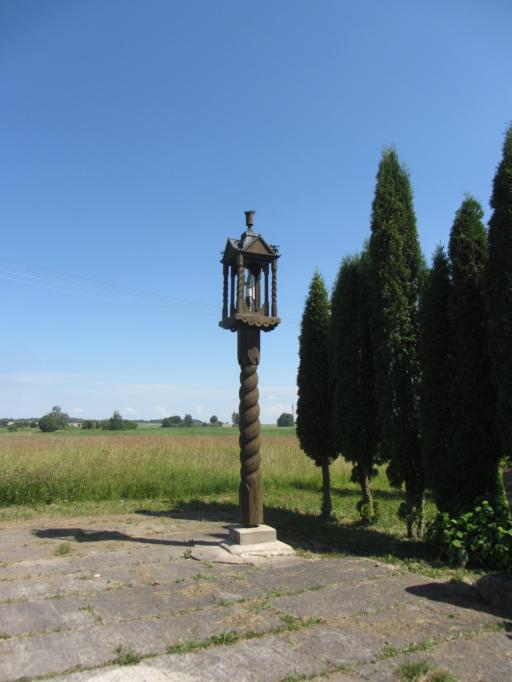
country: LT
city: Sirvintos
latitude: 55.2780
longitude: 25.0155
